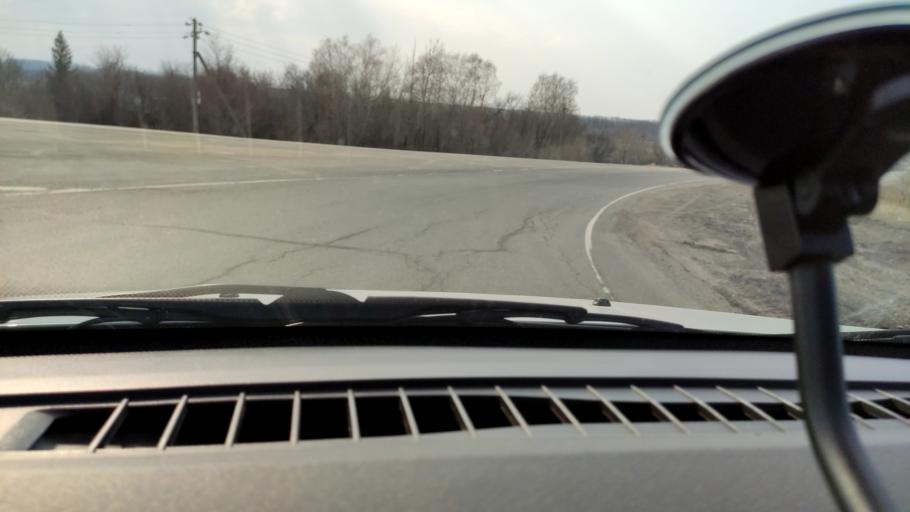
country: RU
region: Samara
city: Dubovyy Umet
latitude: 53.0629
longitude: 50.3760
